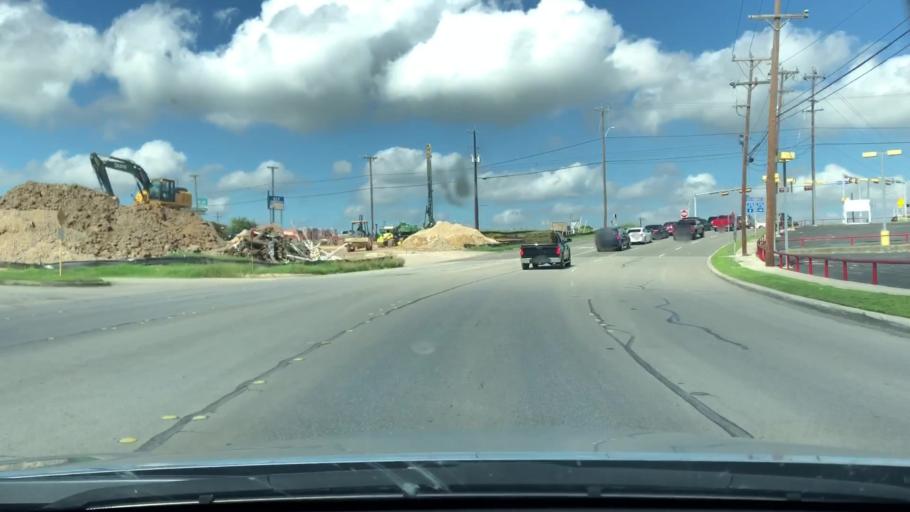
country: US
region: Texas
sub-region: Bexar County
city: Live Oak
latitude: 29.5510
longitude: -98.3542
